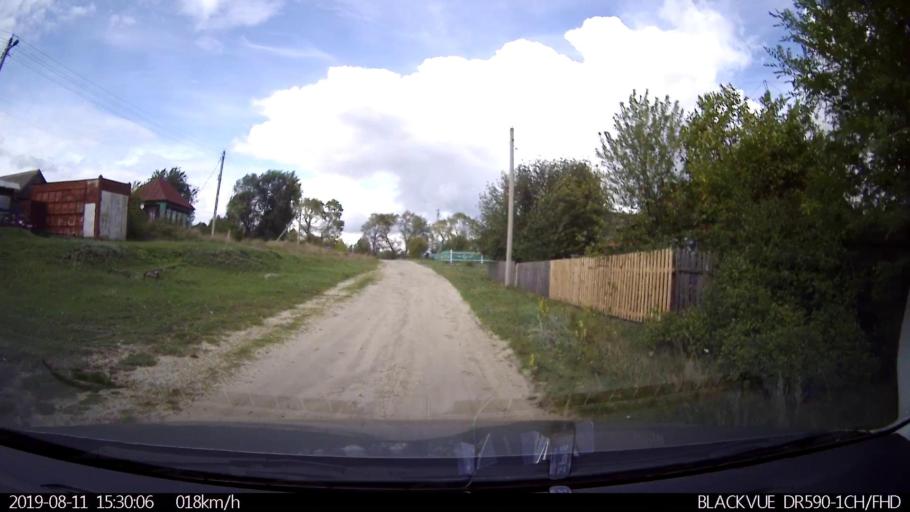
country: RU
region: Ulyanovsk
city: Ignatovka
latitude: 53.8551
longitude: 47.5747
